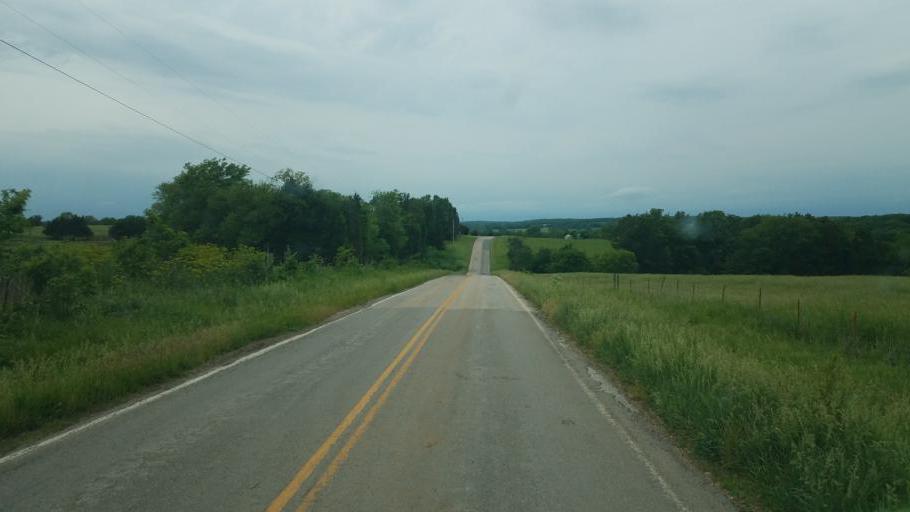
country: US
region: Missouri
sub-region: Moniteau County
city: California
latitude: 38.6841
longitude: -92.6005
